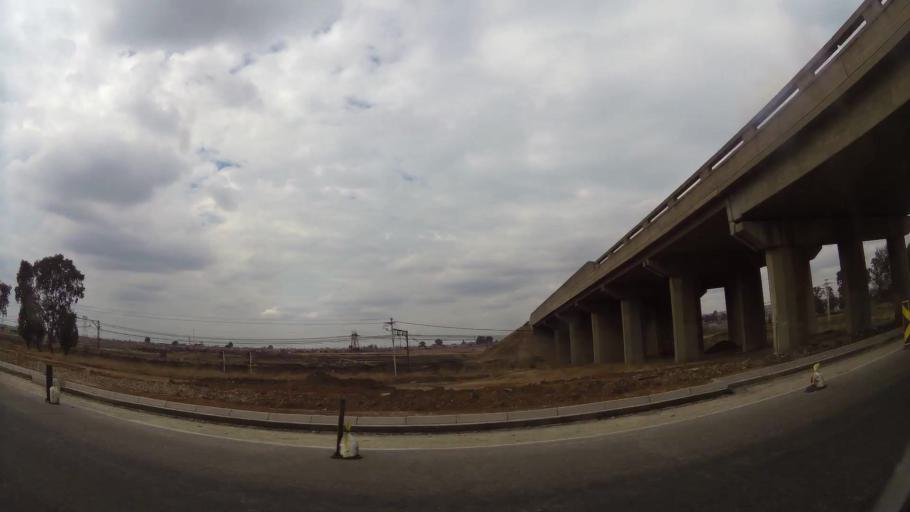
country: ZA
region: Gauteng
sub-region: Ekurhuleni Metropolitan Municipality
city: Germiston
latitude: -26.3643
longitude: 28.1165
